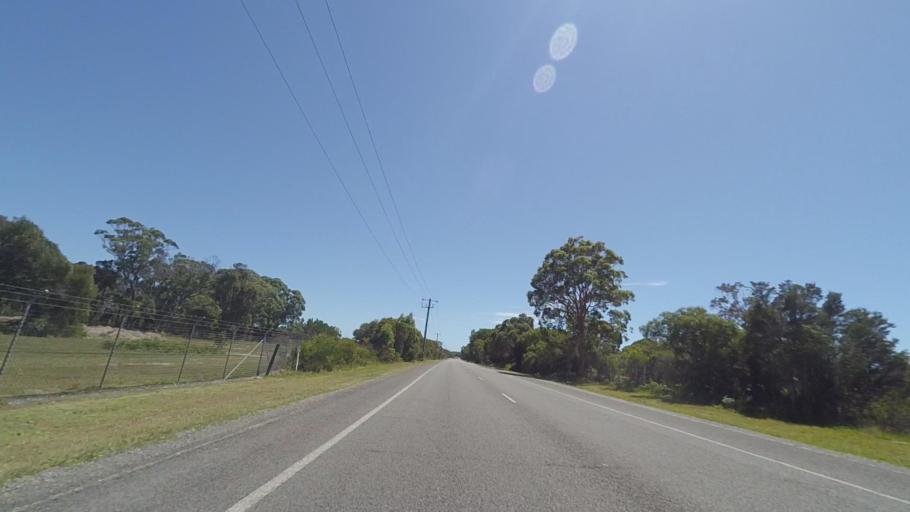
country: AU
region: New South Wales
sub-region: Port Stephens Shire
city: Medowie
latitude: -32.7911
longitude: 151.8540
